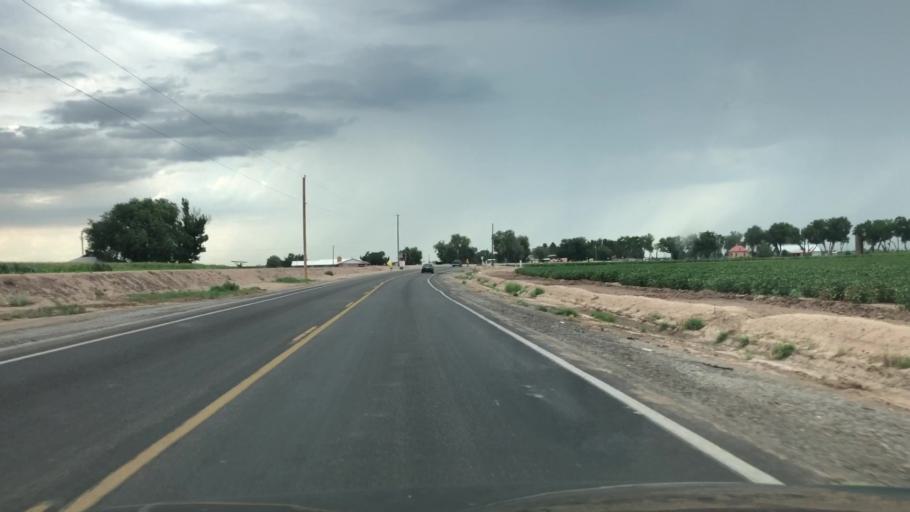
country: US
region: New Mexico
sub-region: Dona Ana County
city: Berino
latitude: 32.0247
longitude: -106.6714
